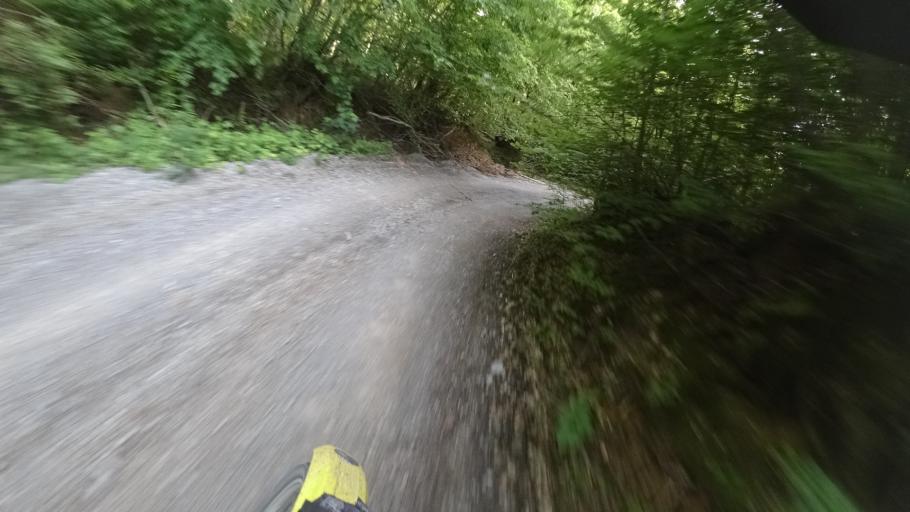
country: HR
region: Licko-Senjska
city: Gospic
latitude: 44.4965
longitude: 15.3057
